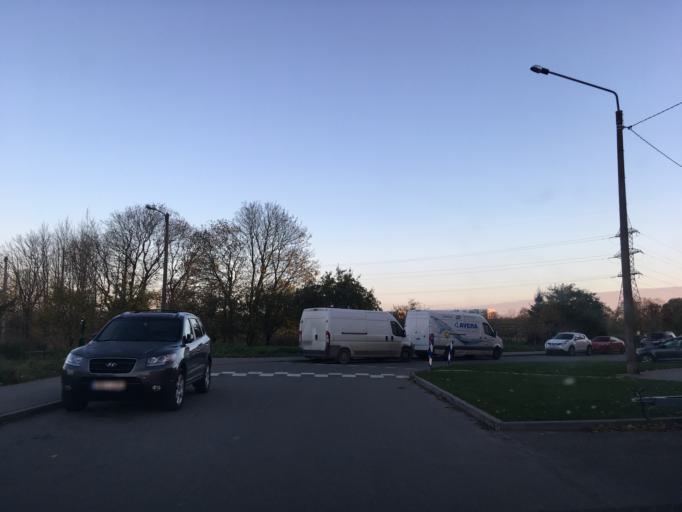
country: EE
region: Harju
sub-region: Viimsi vald
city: Viimsi
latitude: 59.4413
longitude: 24.8199
